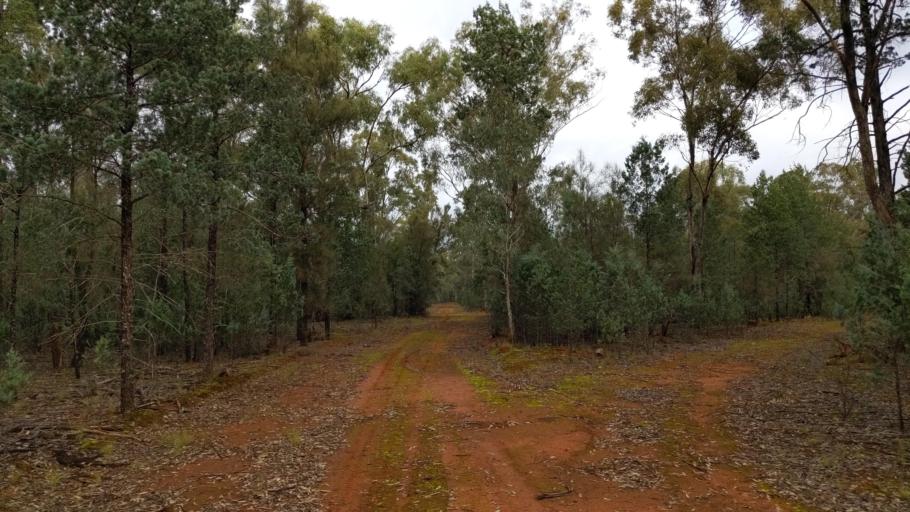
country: AU
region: New South Wales
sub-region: Coolamon
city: Coolamon
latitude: -34.8388
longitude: 146.9340
